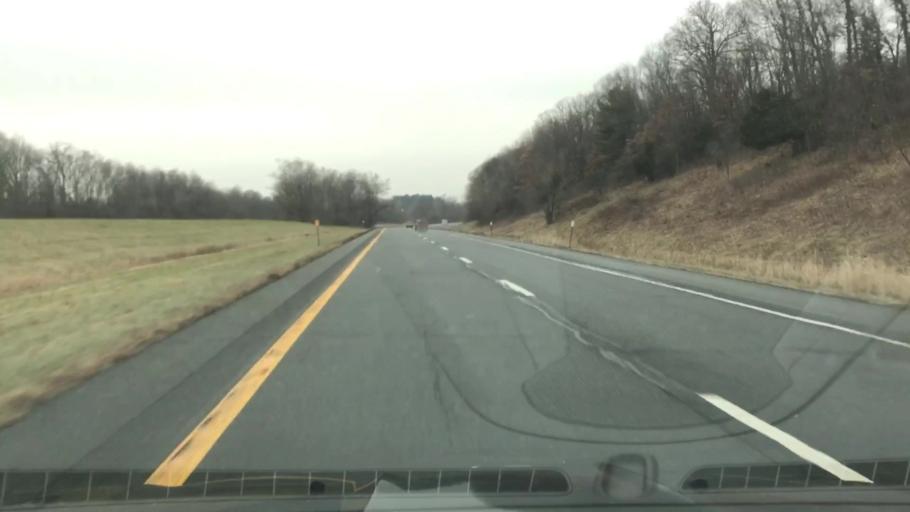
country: US
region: New York
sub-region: Orange County
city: Middletown
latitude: 41.4063
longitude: -74.4609
